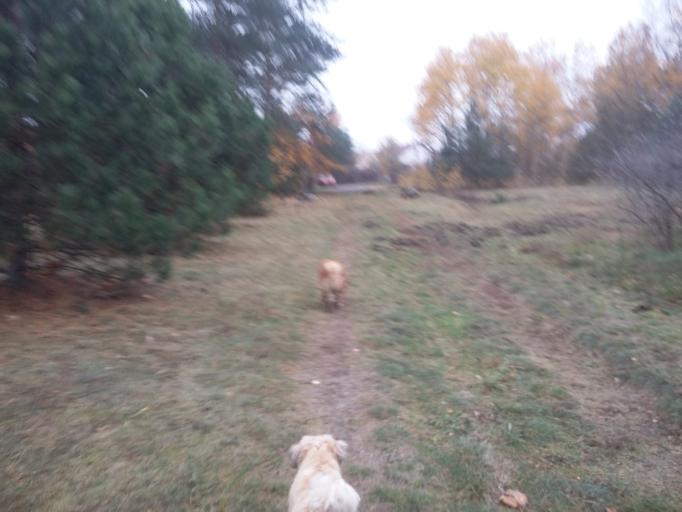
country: PL
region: Lodz Voivodeship
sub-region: Powiat pabianicki
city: Ksawerow
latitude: 51.7298
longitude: 19.3809
